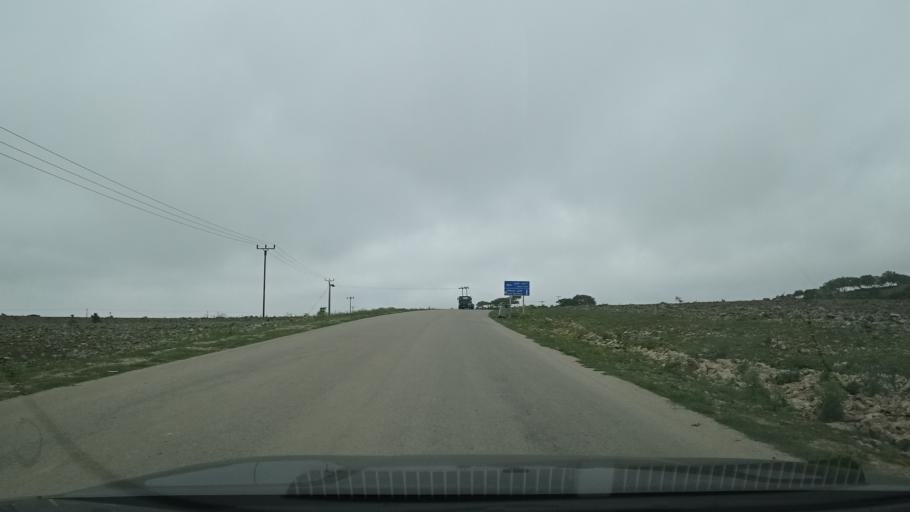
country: OM
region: Zufar
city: Salalah
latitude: 17.1211
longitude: 54.5789
